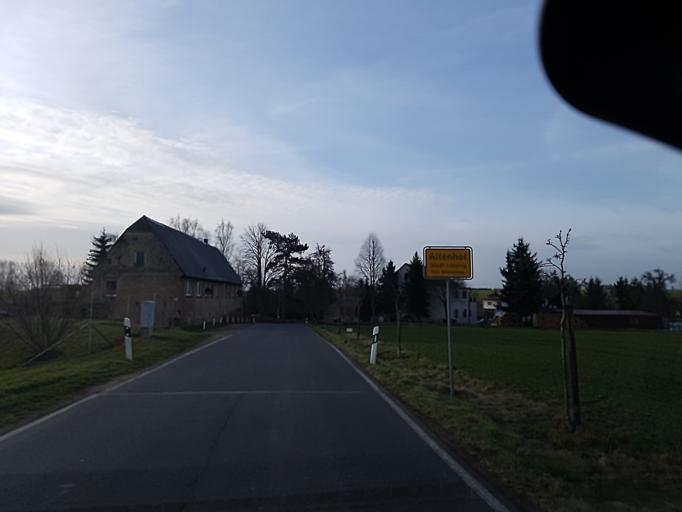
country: DE
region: Saxony
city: Bockelwitz
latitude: 51.1705
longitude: 12.9793
